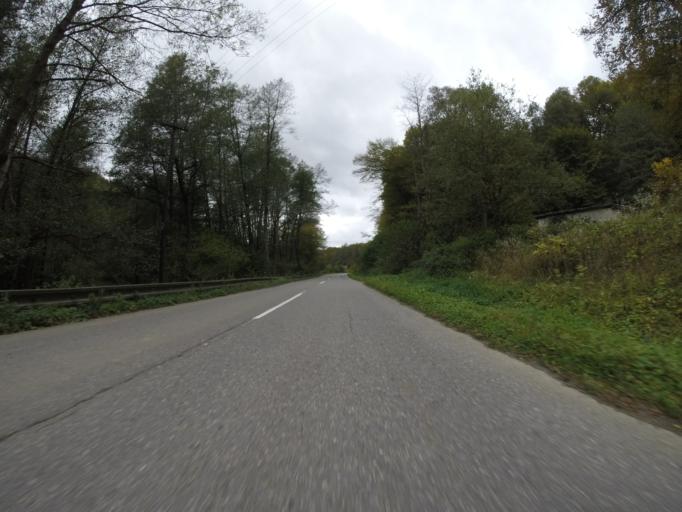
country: SK
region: Banskobystricky
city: Poltar
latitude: 48.5881
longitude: 19.7961
